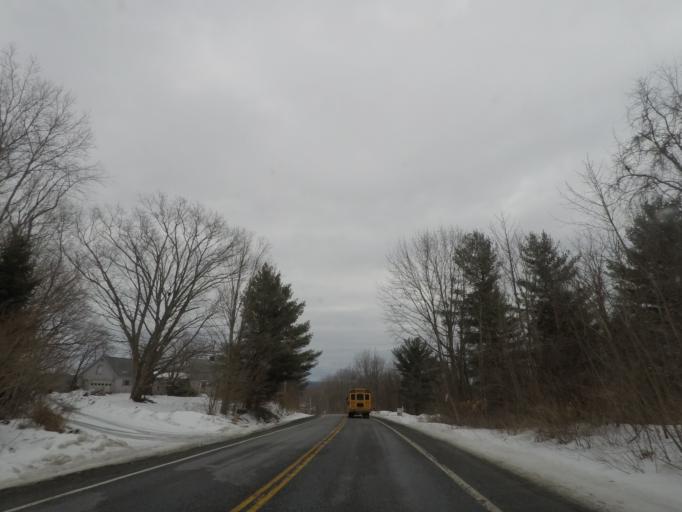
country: US
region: New York
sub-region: Saratoga County
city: Stillwater
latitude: 42.9486
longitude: -73.6652
